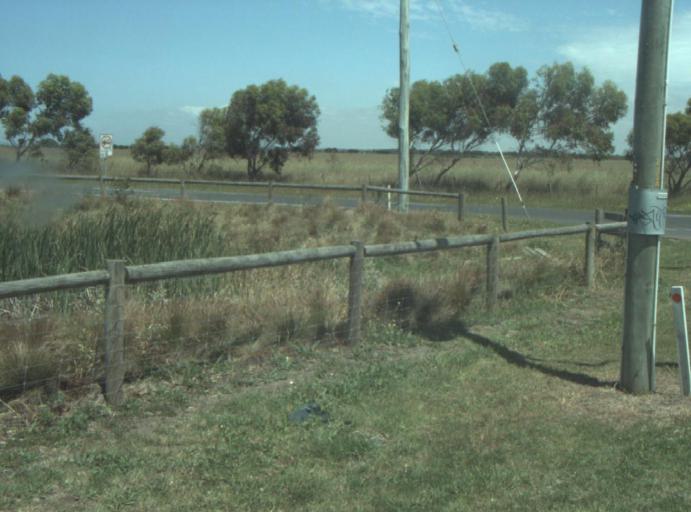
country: AU
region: Victoria
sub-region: Greater Geelong
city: Leopold
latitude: -38.2725
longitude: 144.4224
